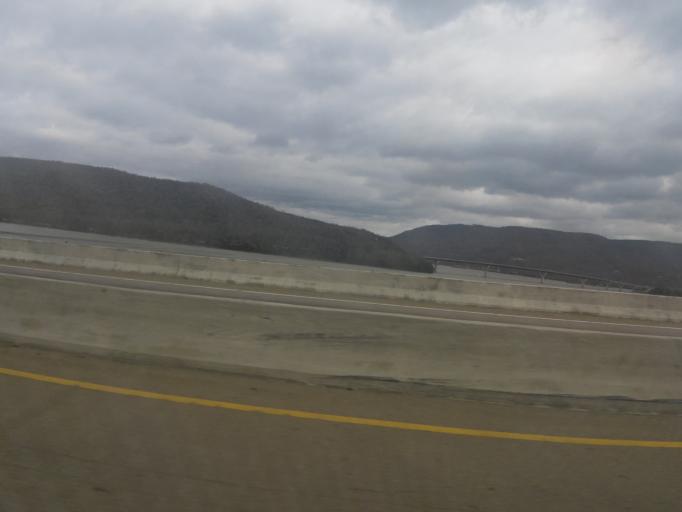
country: US
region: Tennessee
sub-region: Marion County
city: Jasper
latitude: 35.0235
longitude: -85.5539
